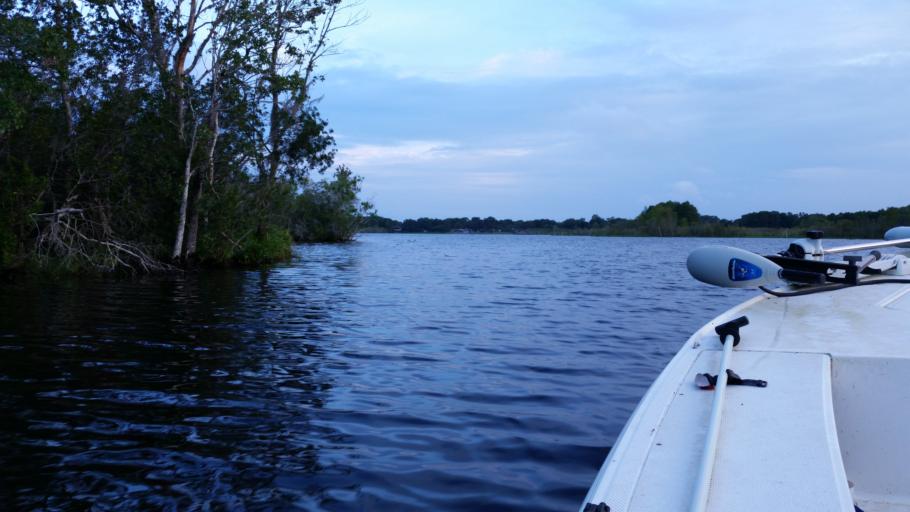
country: US
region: Florida
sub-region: Citrus County
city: Inverness
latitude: 28.8276
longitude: -82.2894
